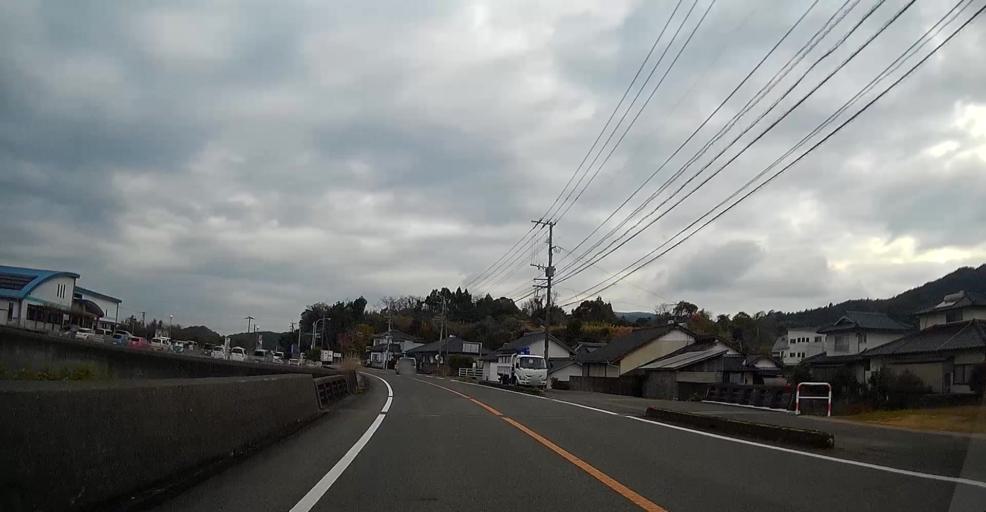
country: JP
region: Kumamoto
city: Hondo
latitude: 32.4601
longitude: 130.2291
